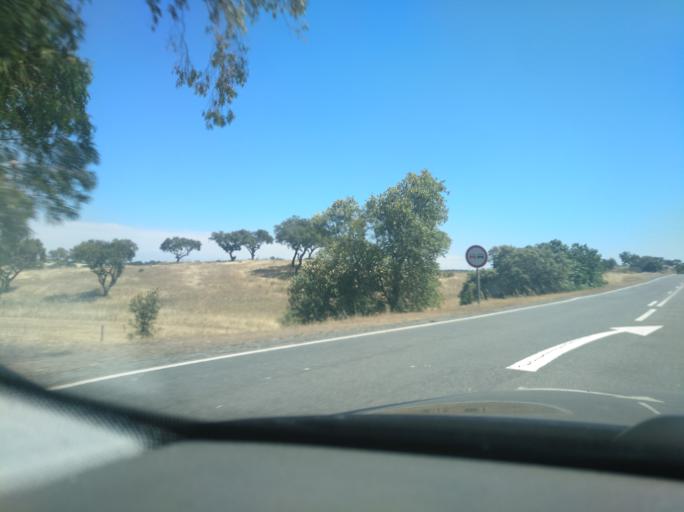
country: PT
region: Beja
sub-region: Castro Verde
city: Castro Verde
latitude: 37.6515
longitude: -8.0813
